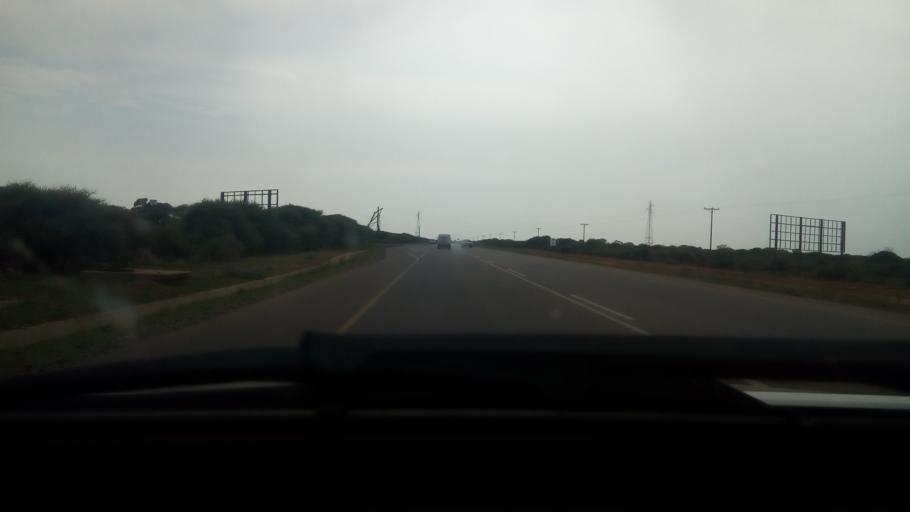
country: BW
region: South East
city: Gaborone
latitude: -24.6714
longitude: 26.0336
